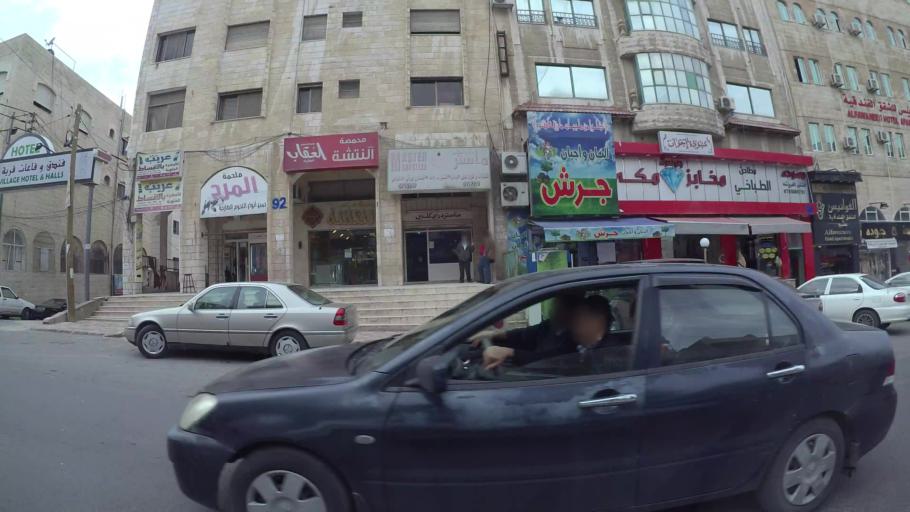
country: JO
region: Amman
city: Umm as Summaq
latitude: 31.8890
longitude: 35.8584
